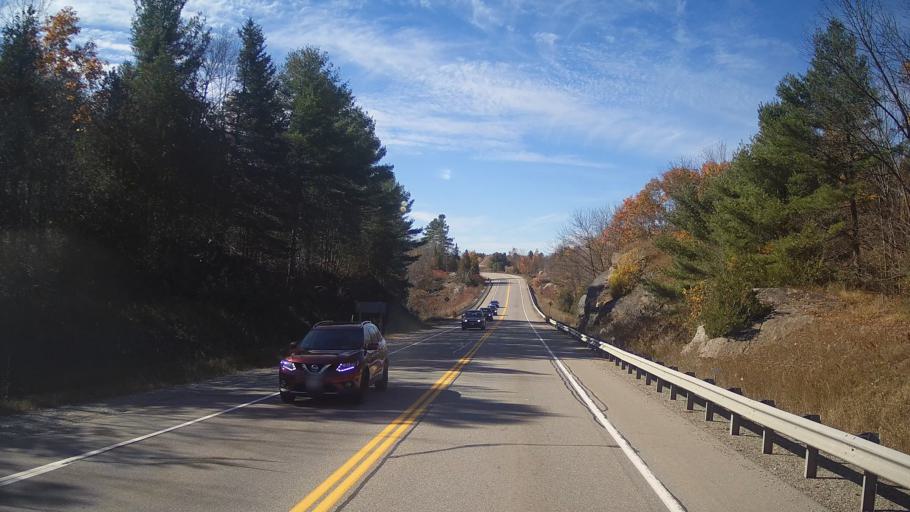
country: CA
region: Ontario
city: Perth
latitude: 44.8036
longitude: -76.6553
